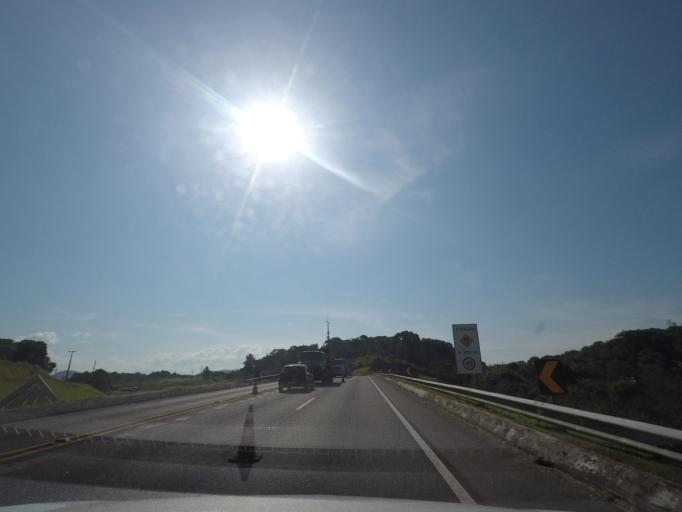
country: BR
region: Parana
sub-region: Paranagua
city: Paranagua
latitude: -25.5695
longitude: -48.6146
